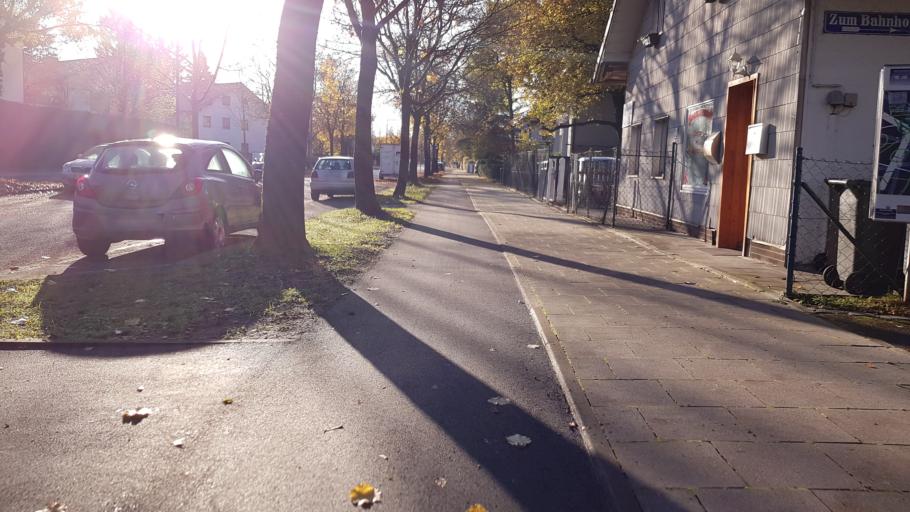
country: DE
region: Bavaria
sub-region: Upper Bavaria
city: Neubiberg
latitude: 48.0960
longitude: 11.6322
